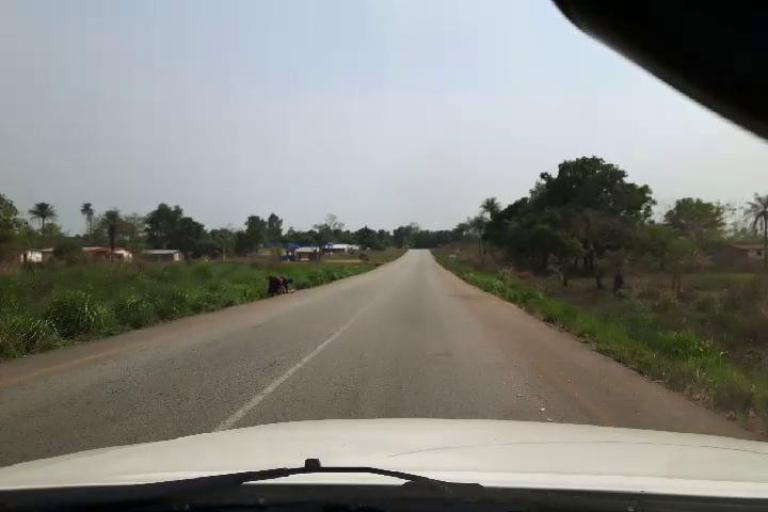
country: SL
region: Southern Province
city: Largo
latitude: 8.3134
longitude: -12.2173
